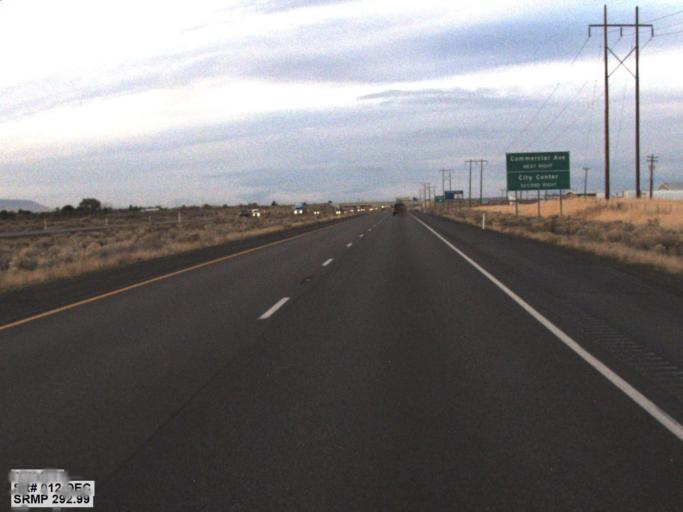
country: US
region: Washington
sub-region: Walla Walla County
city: Burbank
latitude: 46.2334
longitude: -119.0478
